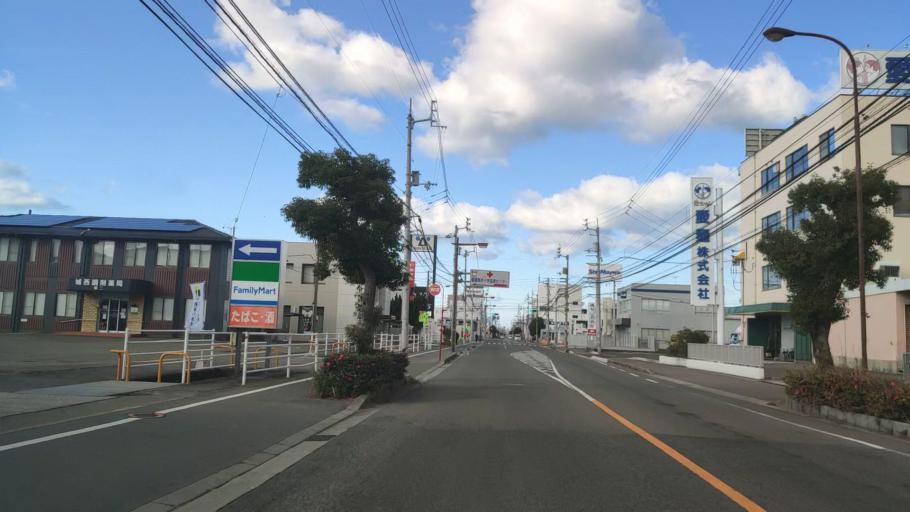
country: JP
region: Ehime
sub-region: Shikoku-chuo Shi
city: Matsuyama
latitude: 33.8284
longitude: 132.7267
